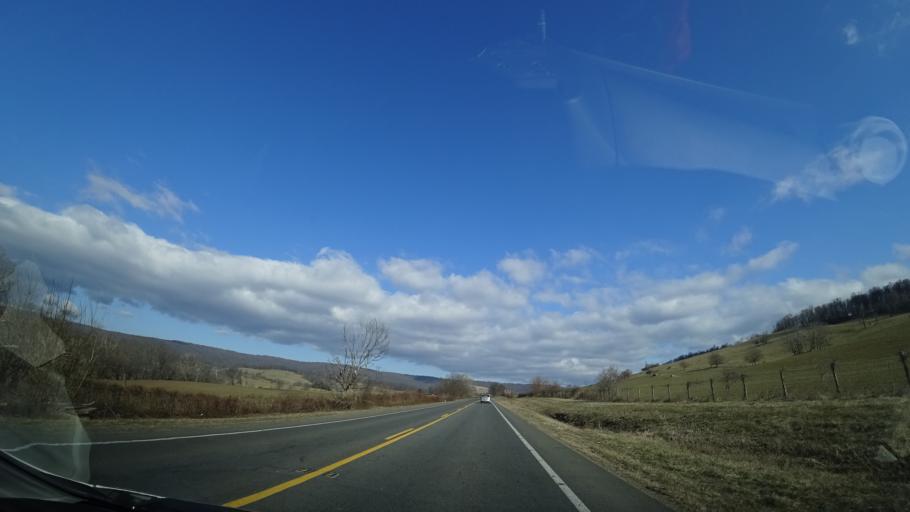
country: US
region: Virginia
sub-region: Warren County
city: Shenandoah Farms
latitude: 38.9666
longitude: -77.9490
